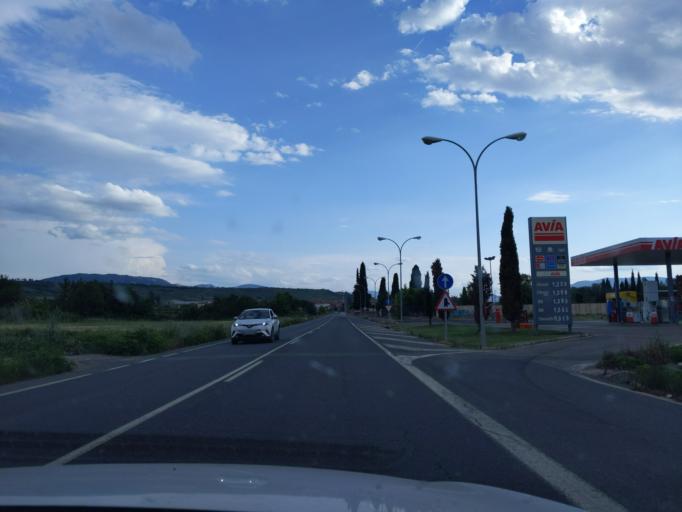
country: ES
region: La Rioja
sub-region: Provincia de La Rioja
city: Alberite
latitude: 42.4135
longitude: -2.4348
